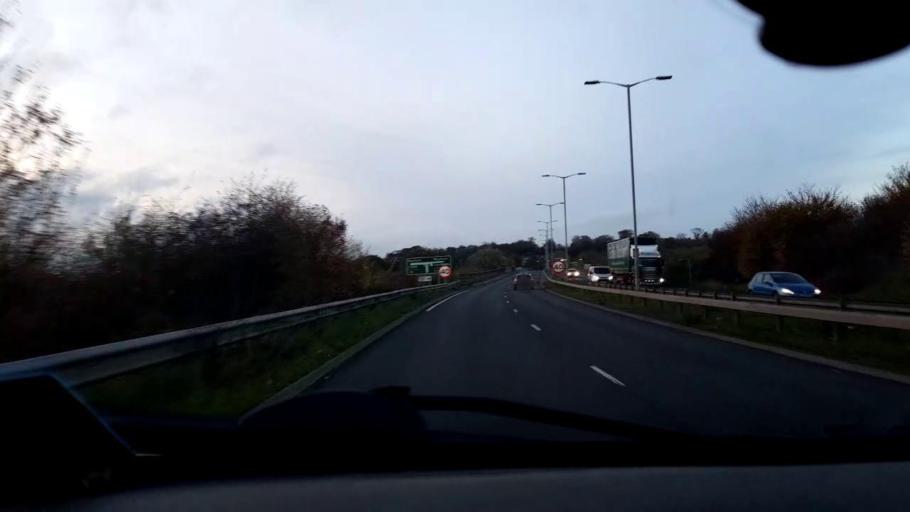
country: GB
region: England
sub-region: Norfolk
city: Thorpe Hamlet
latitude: 52.6095
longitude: 1.3111
